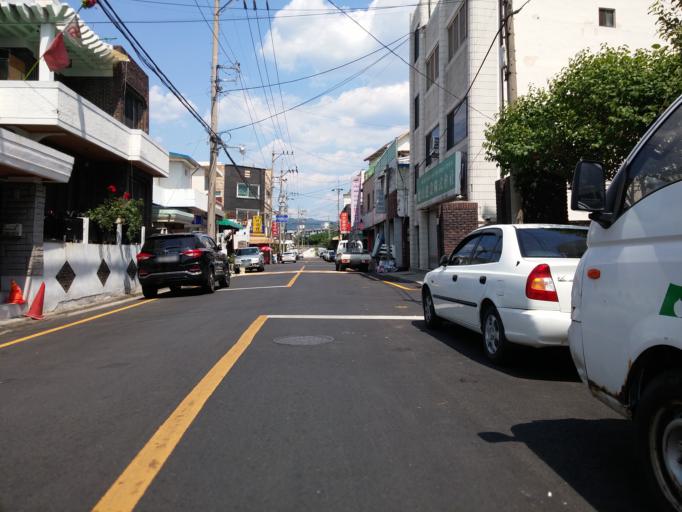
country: KR
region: Chungcheongbuk-do
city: Cheongju-si
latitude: 36.6181
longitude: 127.4900
